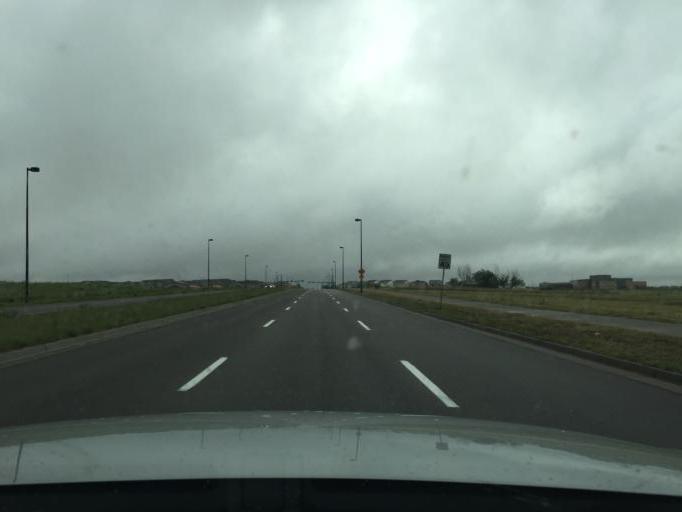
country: US
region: Colorado
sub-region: Adams County
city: Aurora
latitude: 39.7983
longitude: -104.7676
